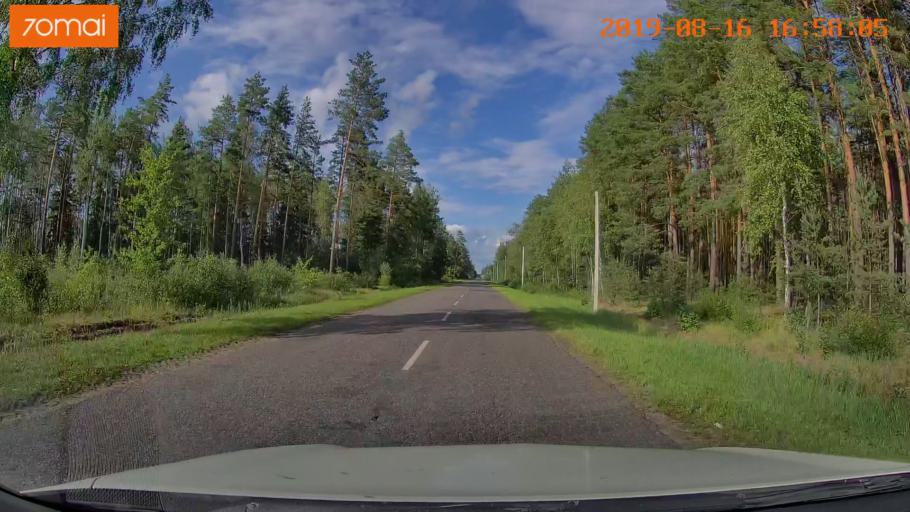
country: BY
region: Mogilev
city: Hlusha
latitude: 53.2645
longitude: 28.8301
